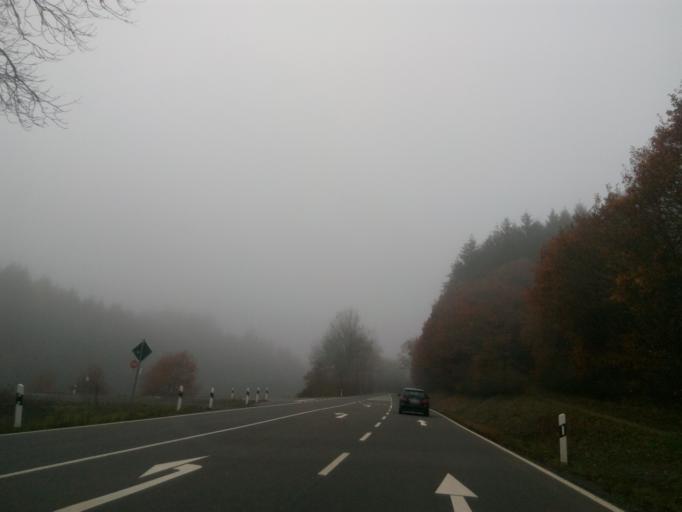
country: DE
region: Rheinland-Pfalz
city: Langweiler
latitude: 49.6804
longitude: 7.5193
